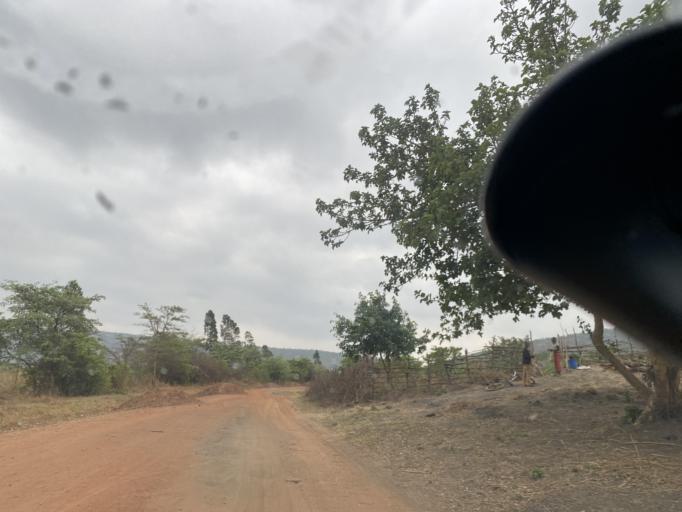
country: ZM
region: Lusaka
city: Chongwe
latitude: -15.1906
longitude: 28.7640
